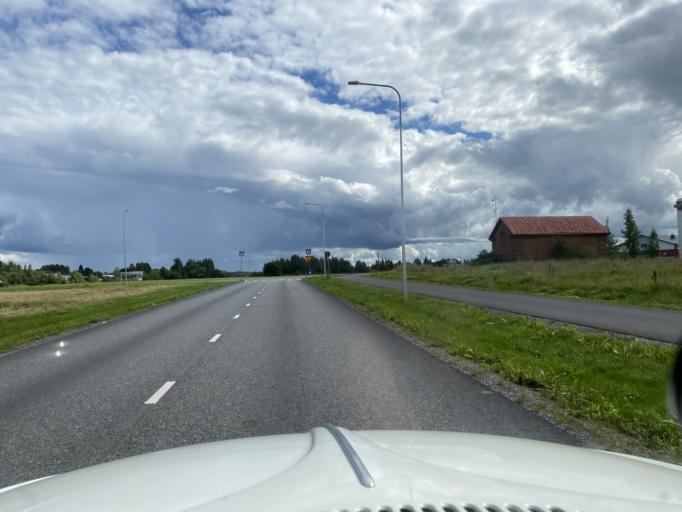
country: FI
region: Satakunta
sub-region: Pori
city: Huittinen
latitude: 61.1705
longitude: 22.6835
